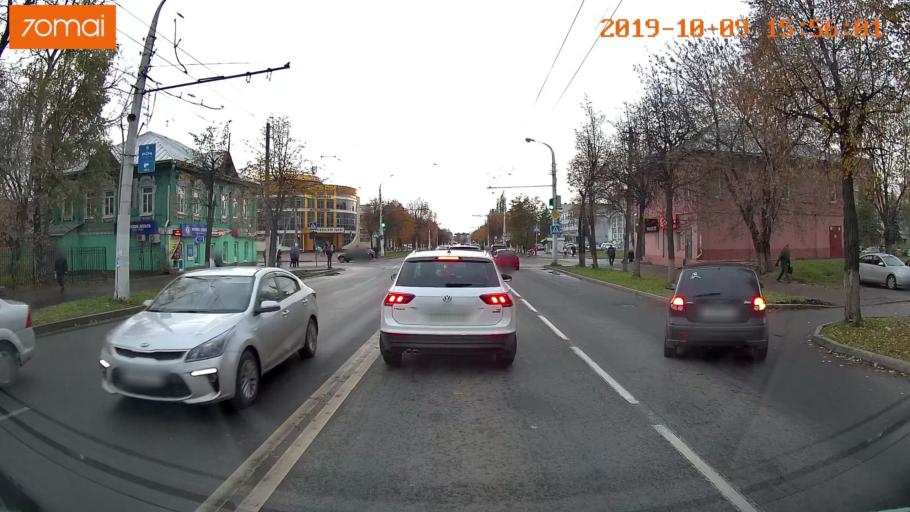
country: RU
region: Kostroma
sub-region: Kostromskoy Rayon
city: Kostroma
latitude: 57.7759
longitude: 40.9435
